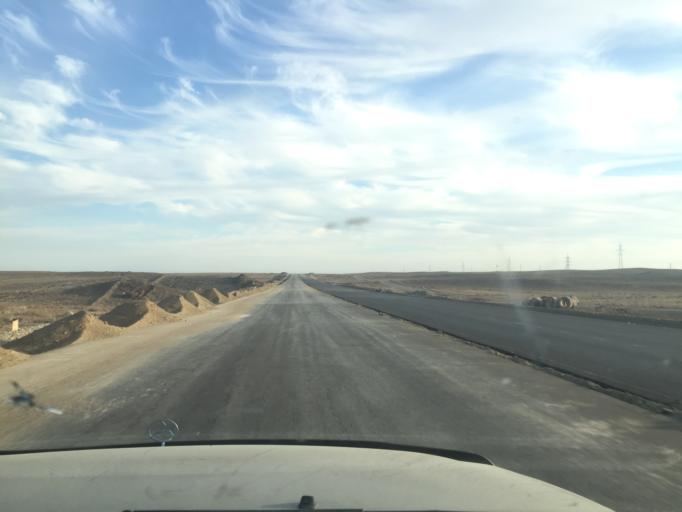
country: KZ
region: Zhambyl
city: Mynaral
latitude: 45.2738
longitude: 73.7860
